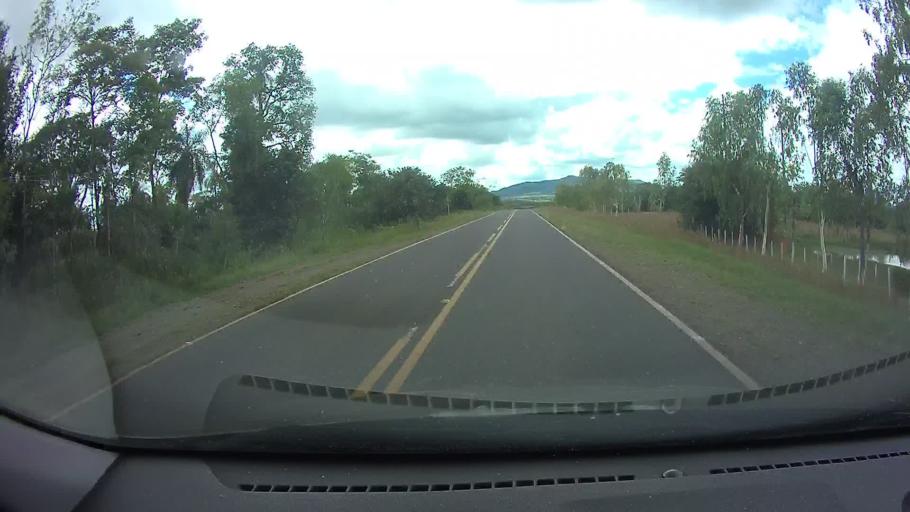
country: PY
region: Paraguari
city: Ybycui
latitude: -25.9134
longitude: -57.0344
